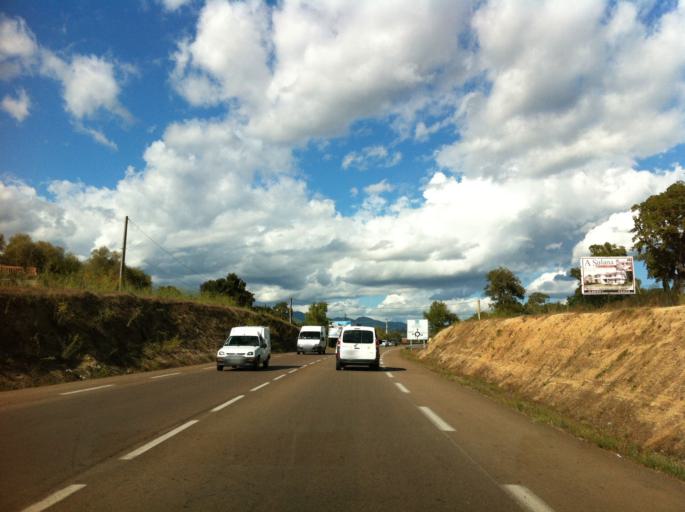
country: FR
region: Corsica
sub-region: Departement de la Corse-du-Sud
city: Porto-Vecchio
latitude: 41.5887
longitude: 9.2626
